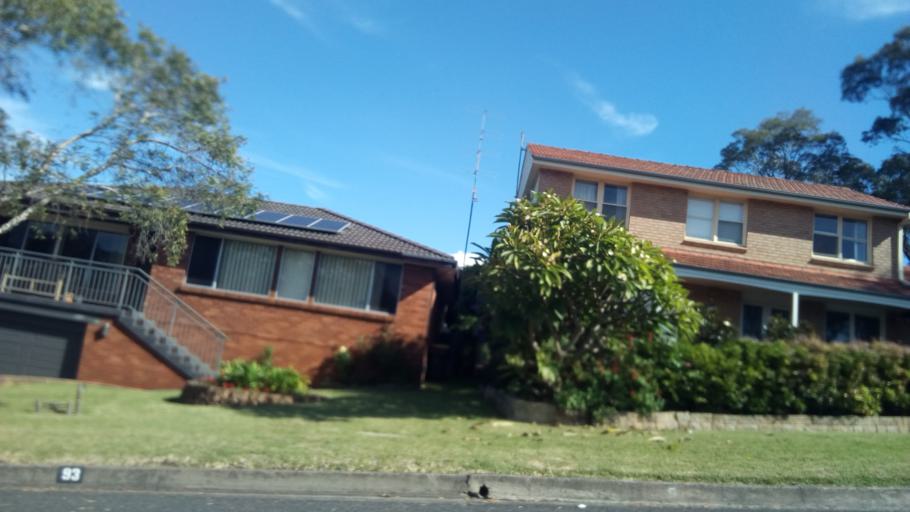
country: AU
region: New South Wales
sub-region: Wollongong
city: Koonawarra
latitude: -34.4942
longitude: 150.8085
